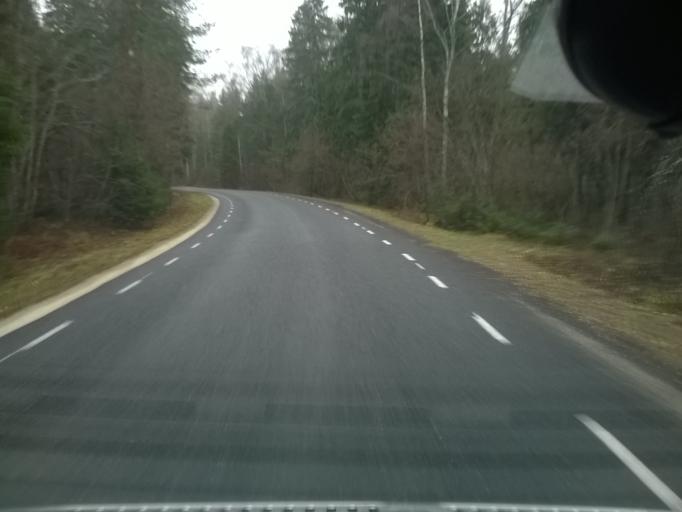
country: EE
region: Harju
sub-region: Saue linn
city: Saue
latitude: 59.1429
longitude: 24.5348
